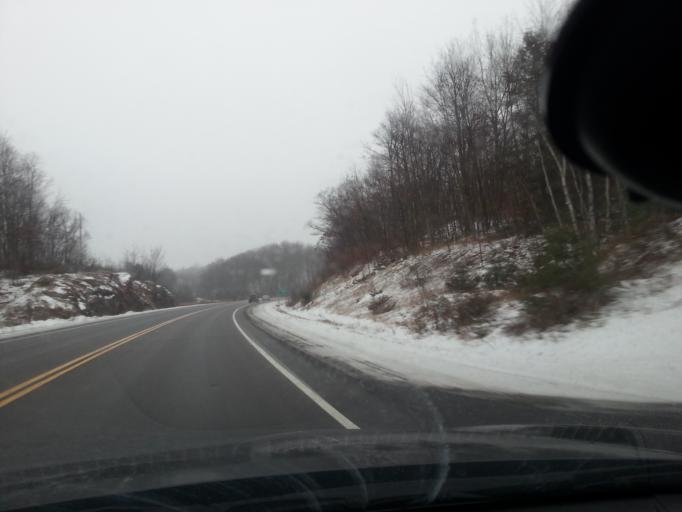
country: CA
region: Ontario
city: Perth
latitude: 44.7806
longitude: -76.7237
